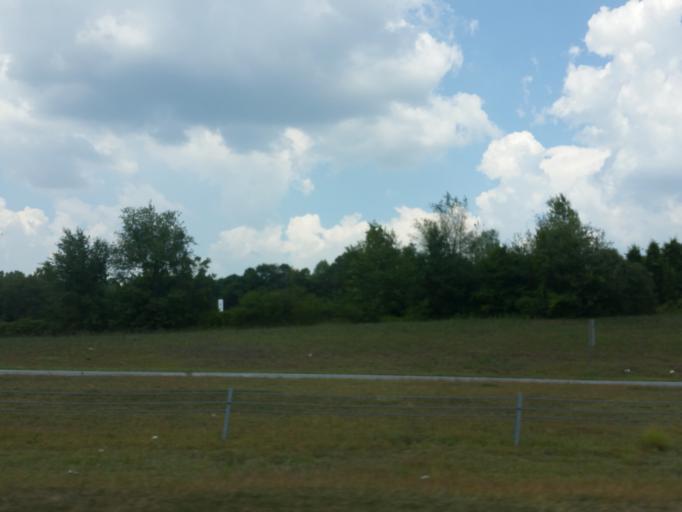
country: US
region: North Carolina
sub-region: Cleveland County
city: White Plains
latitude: 35.2463
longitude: -81.4190
